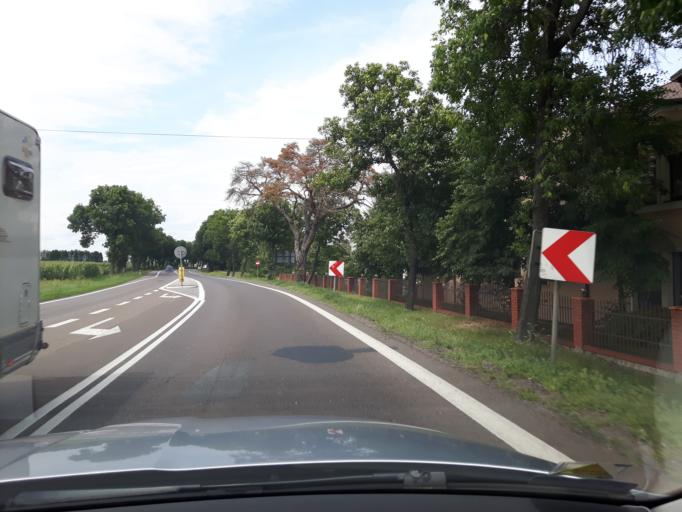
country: PL
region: Masovian Voivodeship
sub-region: Powiat mlawski
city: Strzegowo
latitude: 52.8732
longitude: 20.2912
